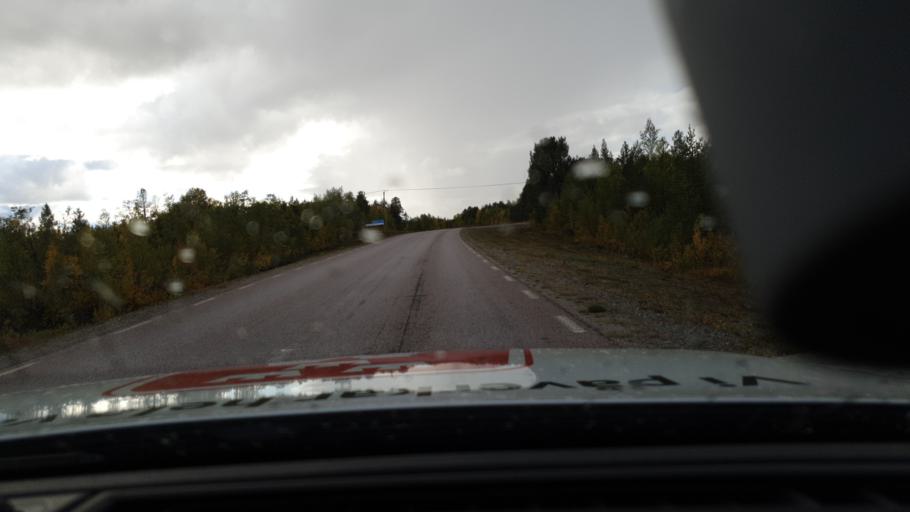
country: NO
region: Finnmark Fylke
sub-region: Kautokeino
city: Kautokeino
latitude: 68.4186
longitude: 22.4111
